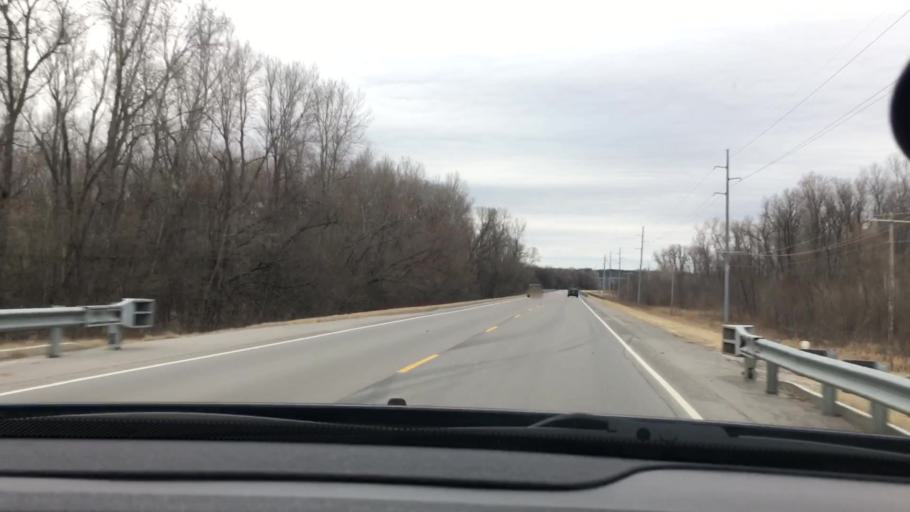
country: US
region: Oklahoma
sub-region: Marshall County
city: Oakland
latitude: 34.2193
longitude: -96.8022
